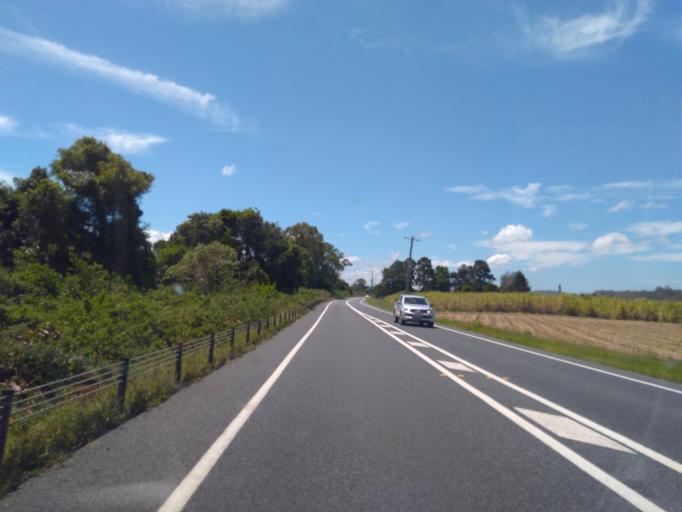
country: AU
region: New South Wales
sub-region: Clarence Valley
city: Maclean
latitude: -29.5249
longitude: 153.1859
